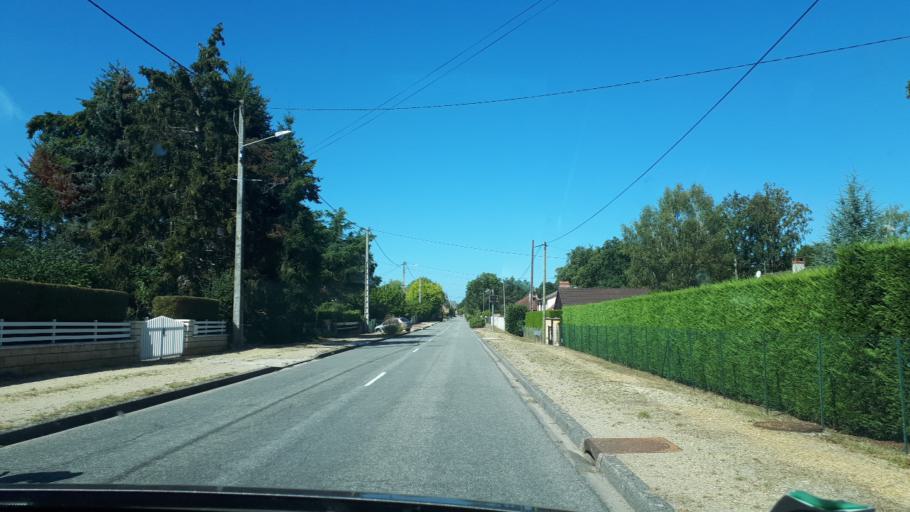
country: FR
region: Centre
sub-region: Departement du Loiret
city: Cerdon
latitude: 47.6370
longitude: 2.3742
